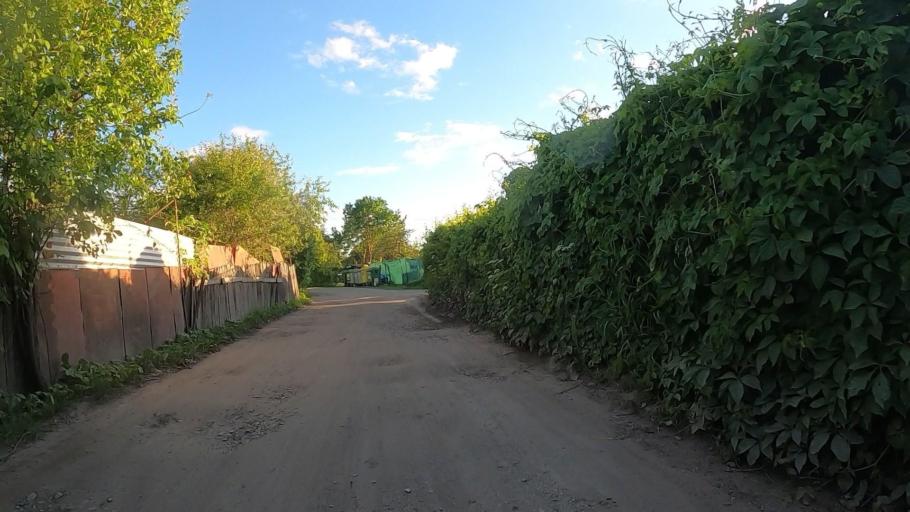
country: LV
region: Kekava
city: Kekava
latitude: 56.8826
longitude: 24.2204
